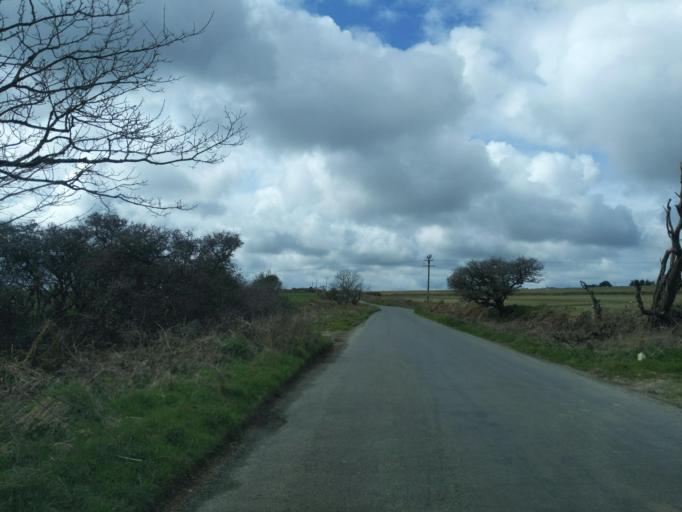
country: GB
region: England
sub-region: Cornwall
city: Camelford
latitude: 50.6407
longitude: -4.6364
